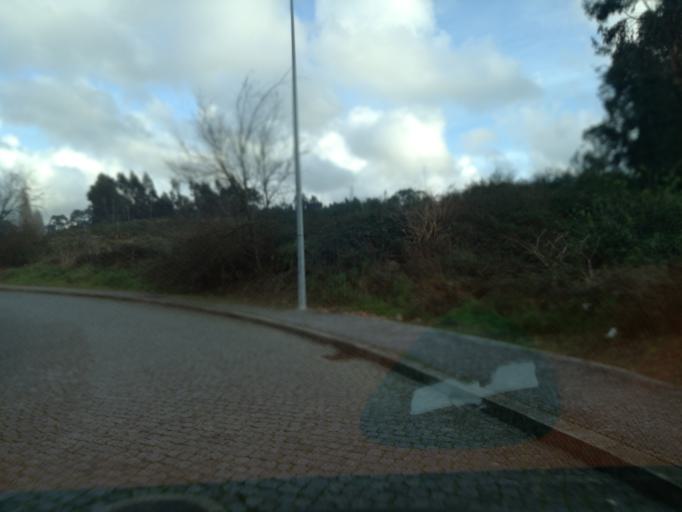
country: PT
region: Porto
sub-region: Maia
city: Nogueira
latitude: 41.2526
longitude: -8.6021
